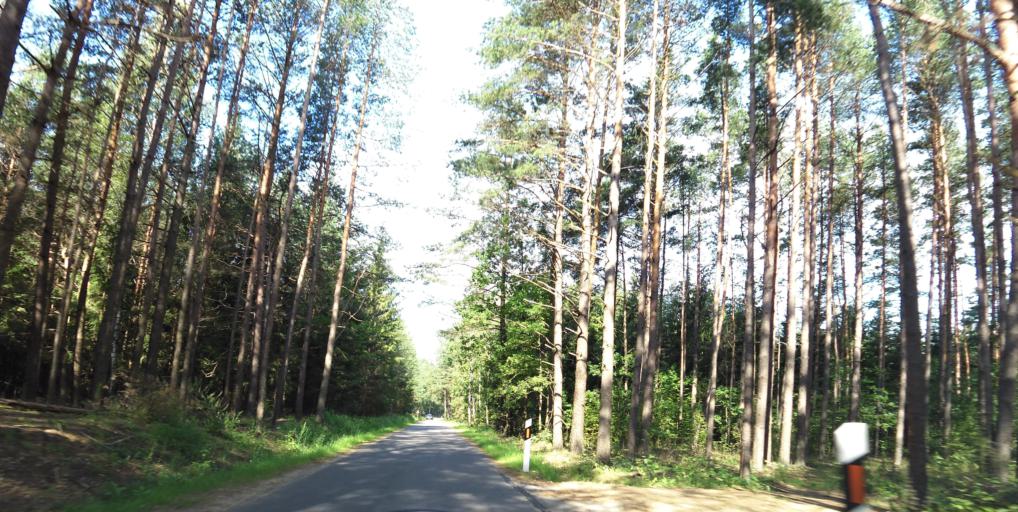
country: LT
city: Grigiskes
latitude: 54.7244
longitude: 25.0523
